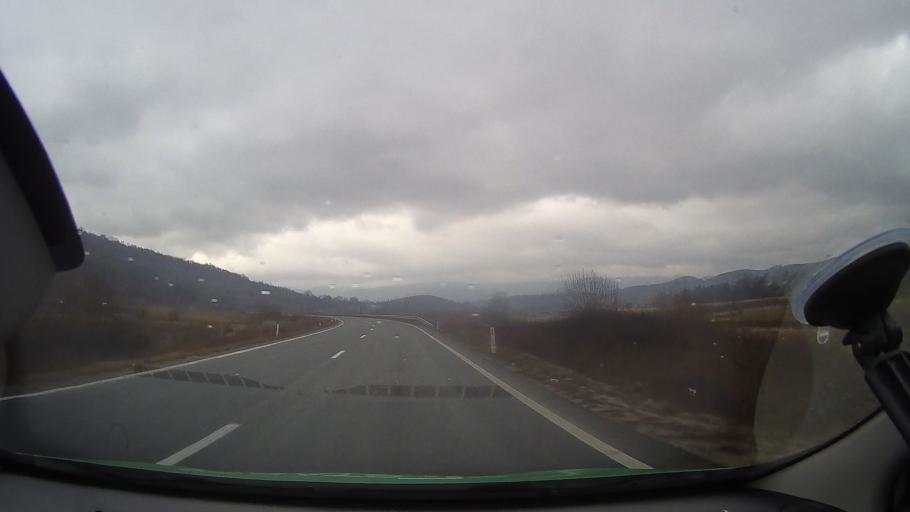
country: RO
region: Hunedoara
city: Vata de Jos
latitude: 46.2158
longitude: 22.5767
